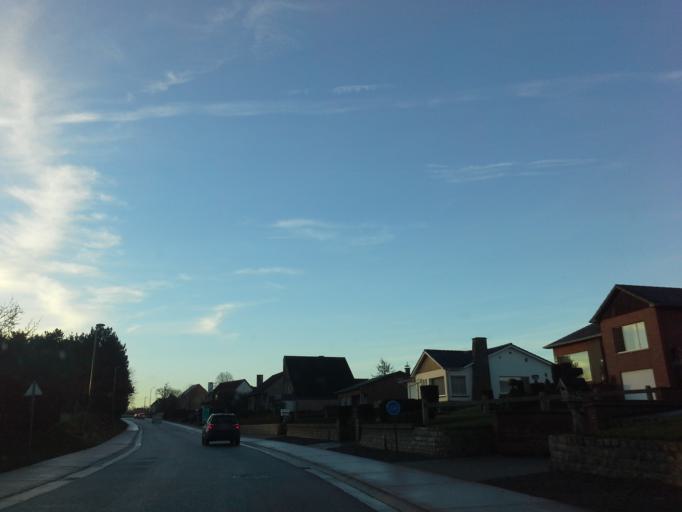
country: BE
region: Flanders
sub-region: Provincie Vlaams-Brabant
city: Bekkevoort
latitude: 50.9420
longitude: 4.9551
